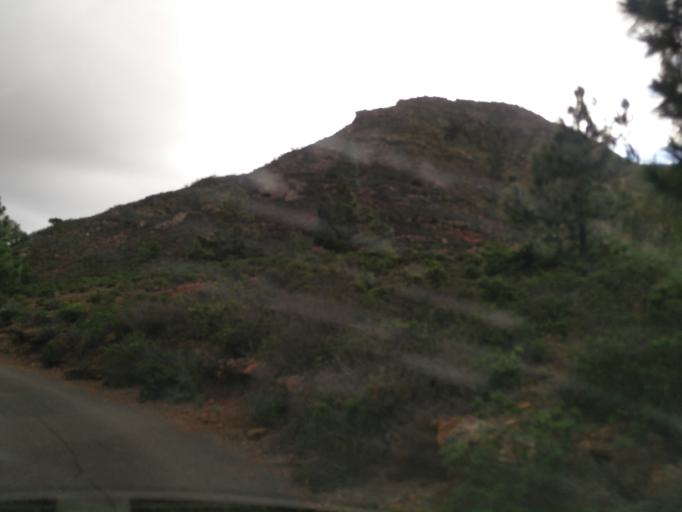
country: ES
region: Canary Islands
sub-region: Provincia de Santa Cruz de Tenerife
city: Arona
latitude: 28.1261
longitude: -16.6920
